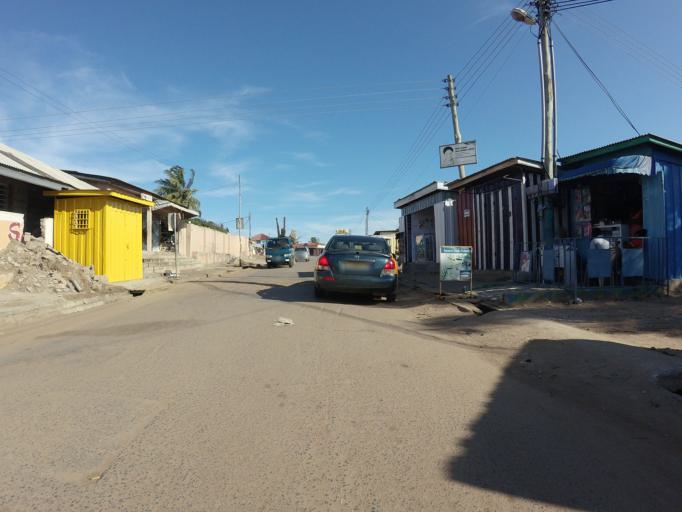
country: GH
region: Greater Accra
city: Nungua
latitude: 5.5906
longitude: -0.0823
